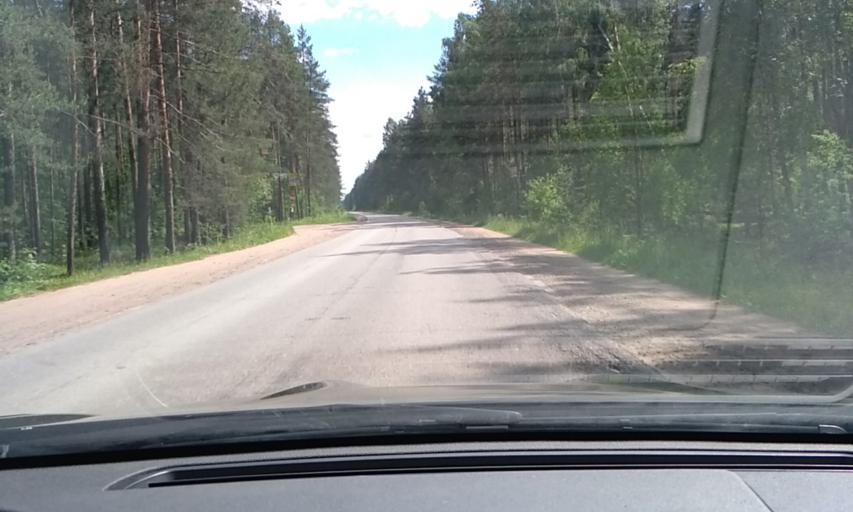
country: RU
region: Leningrad
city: Imeni Sverdlova
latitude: 59.8423
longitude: 30.6904
